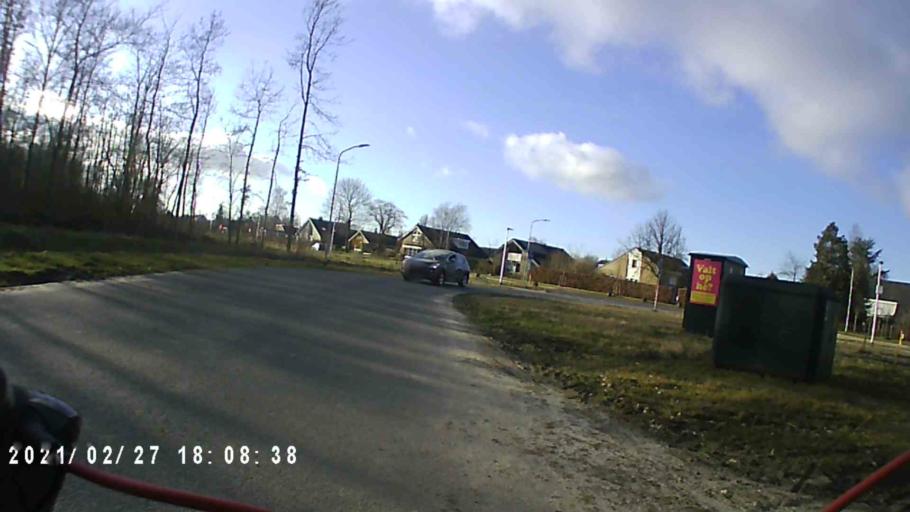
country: NL
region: Groningen
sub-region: Gemeente Bedum
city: Bedum
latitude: 53.2938
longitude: 6.6040
